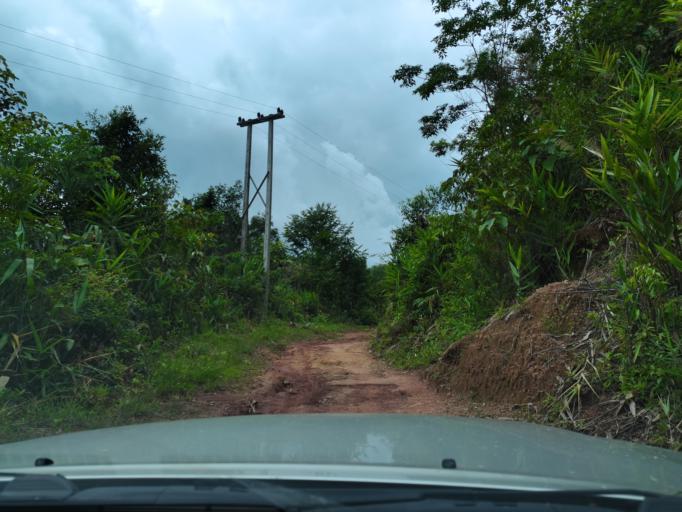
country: LA
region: Loungnamtha
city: Muang Nale
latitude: 20.5065
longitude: 101.0830
